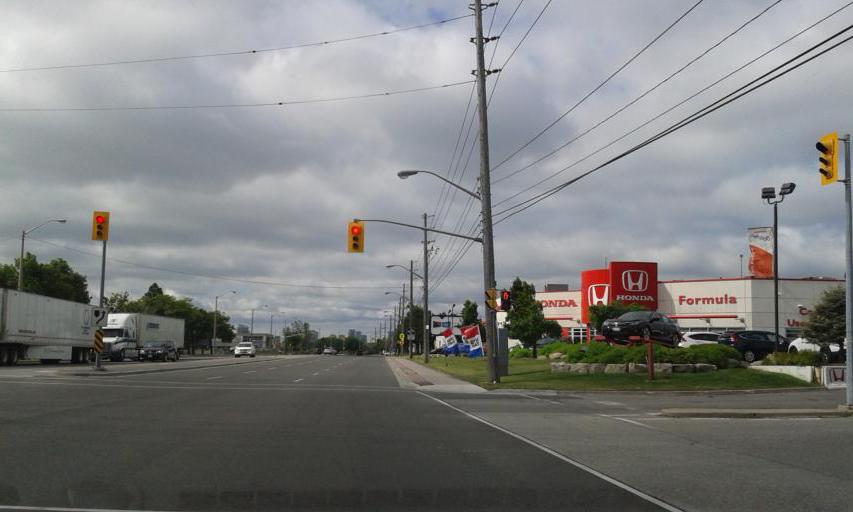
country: CA
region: Ontario
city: Scarborough
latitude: 43.8109
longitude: -79.2430
